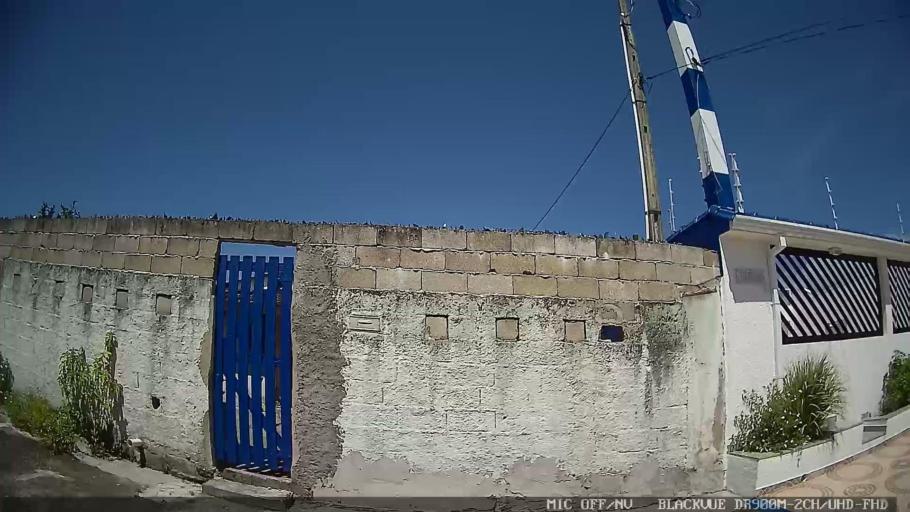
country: BR
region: Sao Paulo
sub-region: Peruibe
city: Peruibe
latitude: -24.3050
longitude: -46.9951
